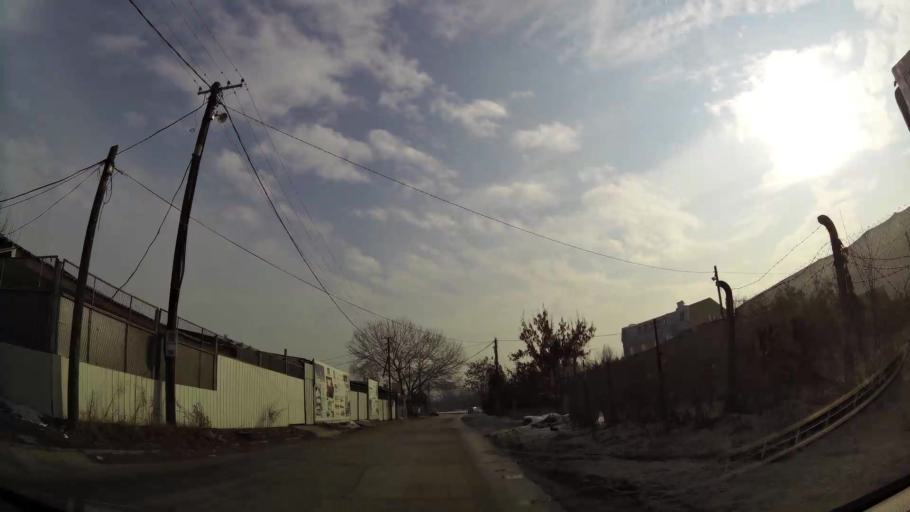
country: MK
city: Krushopek
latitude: 42.0128
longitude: 21.3783
